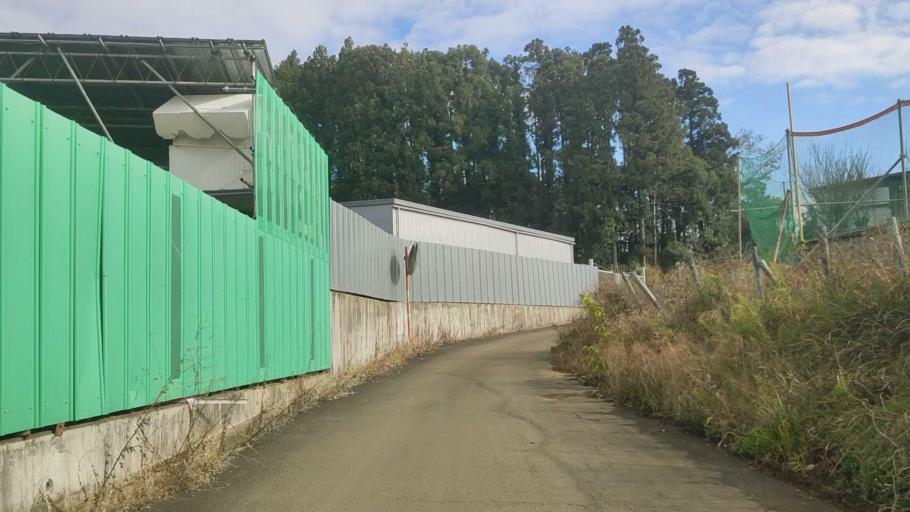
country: JP
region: Kanagawa
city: Minami-rinkan
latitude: 35.4868
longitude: 139.4958
